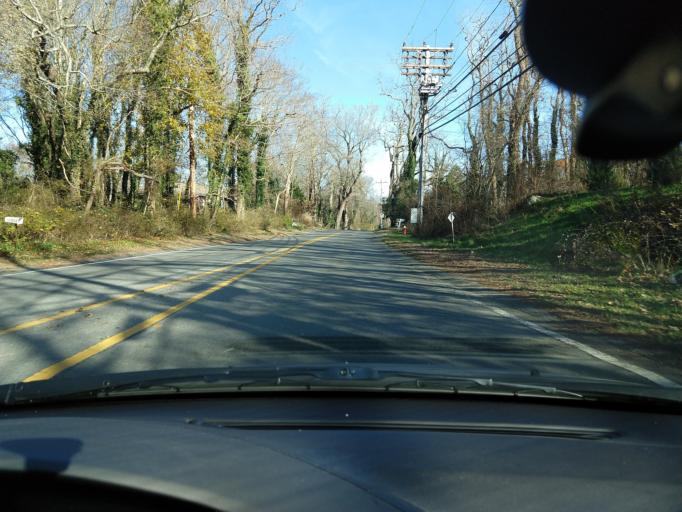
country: US
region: Massachusetts
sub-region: Barnstable County
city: West Barnstable
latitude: 41.6961
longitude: -70.3438
